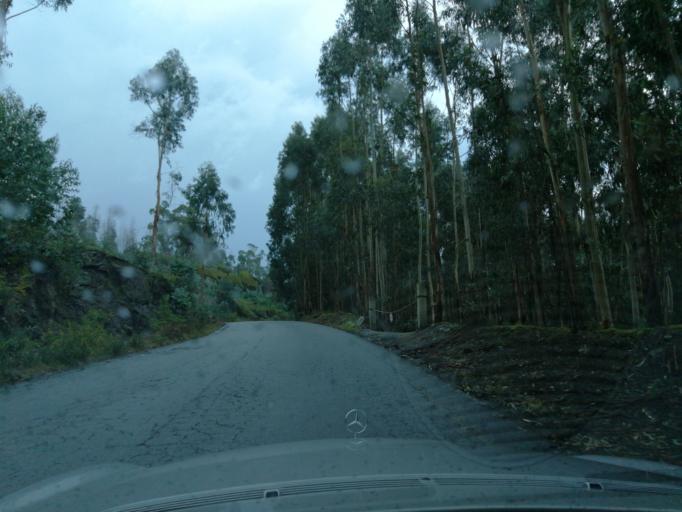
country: PT
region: Braga
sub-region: Braga
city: Oliveira
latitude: 41.4662
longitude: -8.4374
